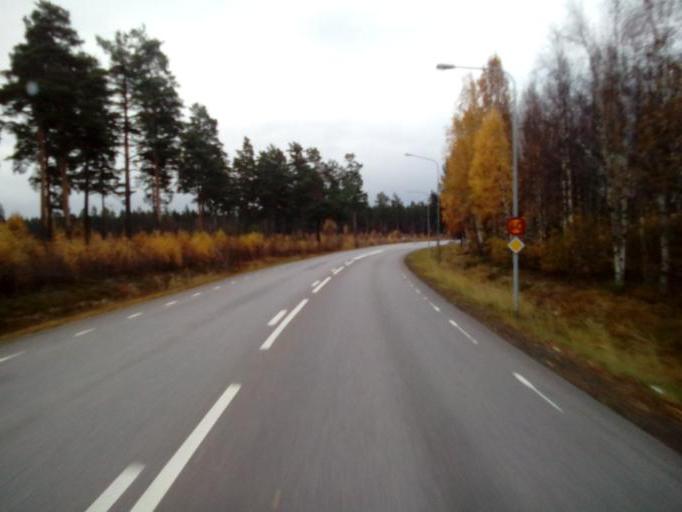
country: SE
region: OErebro
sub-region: Laxa Kommun
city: Laxa
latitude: 58.9883
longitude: 14.6337
